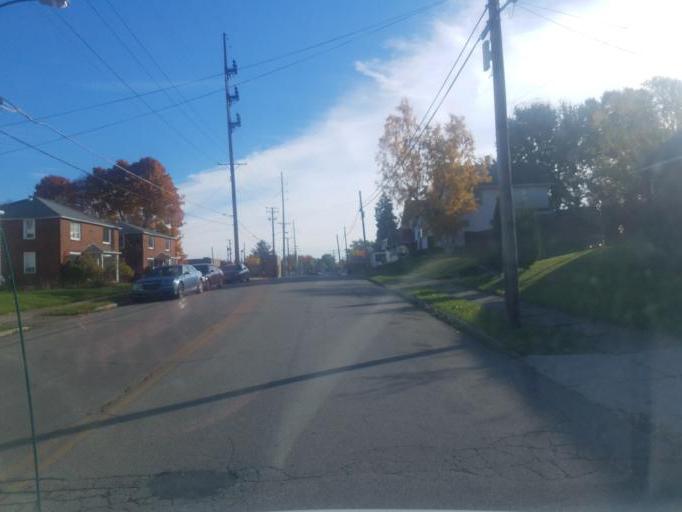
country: US
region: Ohio
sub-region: Richland County
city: Mansfield
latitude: 40.7476
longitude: -82.5245
